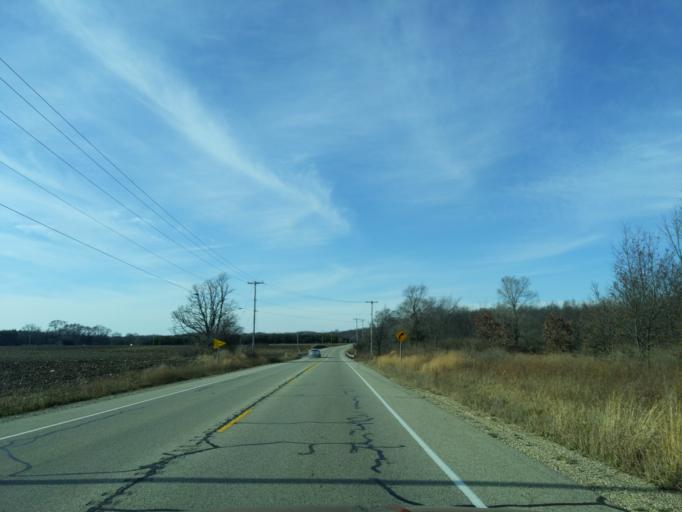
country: US
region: Wisconsin
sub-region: Jefferson County
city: Palmyra
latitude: 42.7970
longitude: -88.6354
